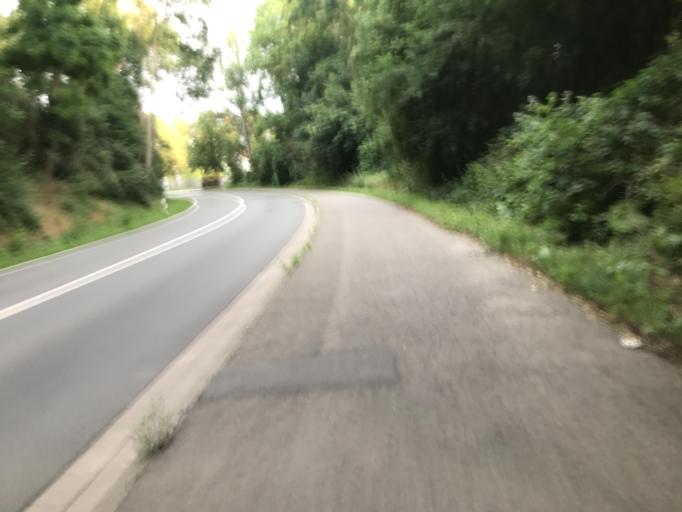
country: DE
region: Saxony-Anhalt
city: Quedlinburg
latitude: 51.8015
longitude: 11.1314
